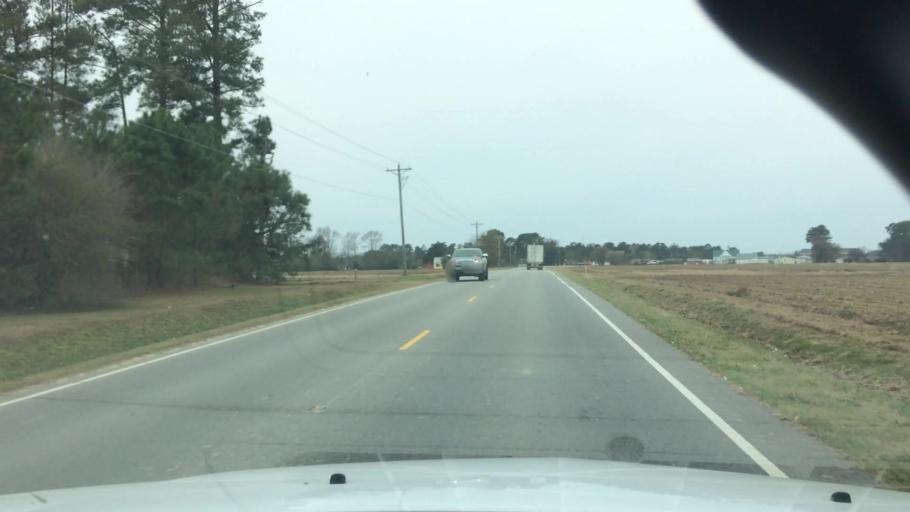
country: US
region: North Carolina
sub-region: Greene County
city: Maury
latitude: 35.4699
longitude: -77.5379
